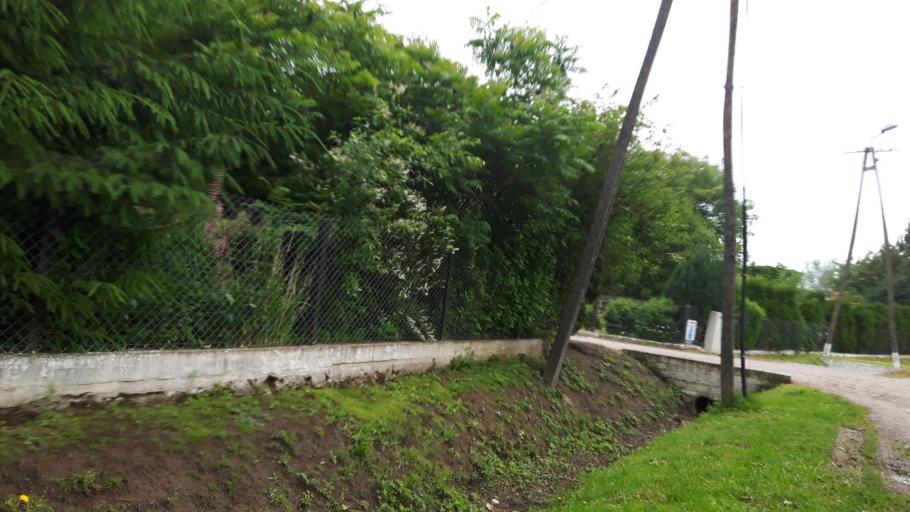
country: PL
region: West Pomeranian Voivodeship
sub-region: Powiat koszalinski
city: Sianow
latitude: 54.2969
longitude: 16.2762
